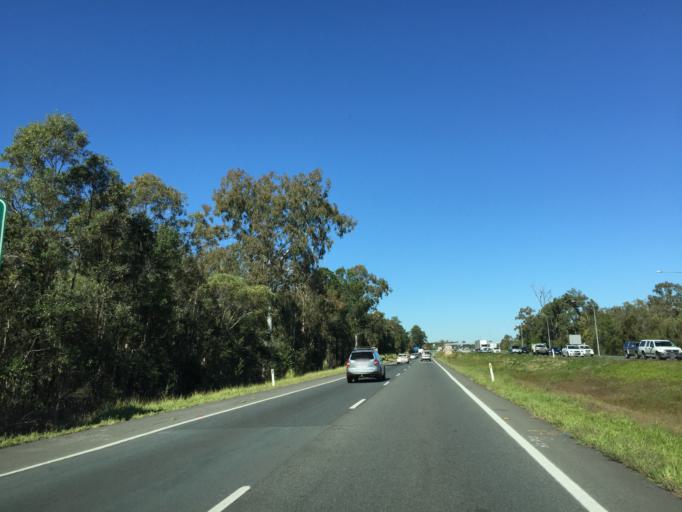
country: AU
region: Queensland
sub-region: Moreton Bay
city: Caboolture
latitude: -27.0626
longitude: 152.9775
